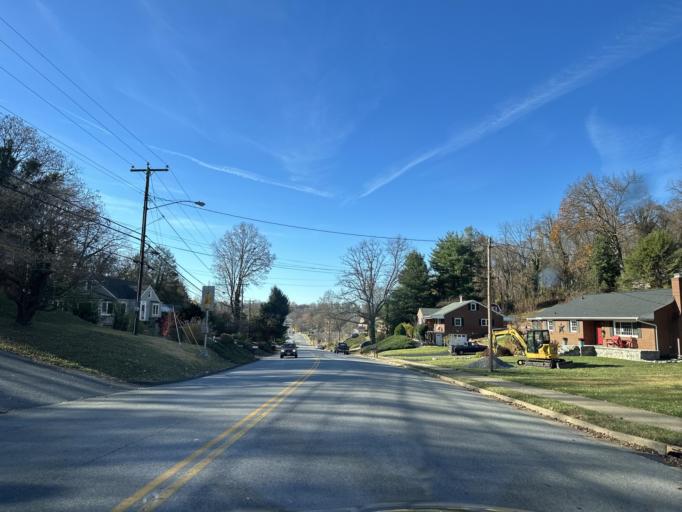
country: US
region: Virginia
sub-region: City of Staunton
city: Staunton
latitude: 38.1623
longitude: -79.0598
